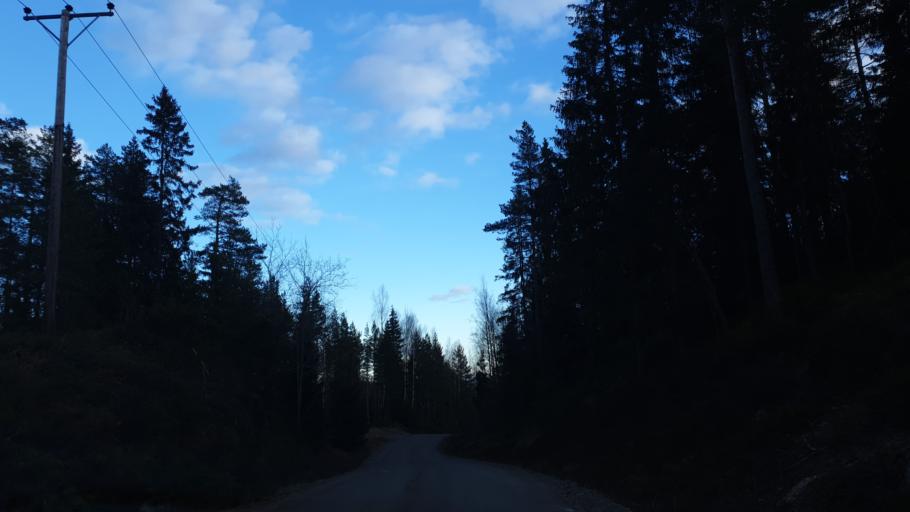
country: SE
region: OErebro
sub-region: Orebro Kommun
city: Garphyttan
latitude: 59.3665
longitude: 14.9671
